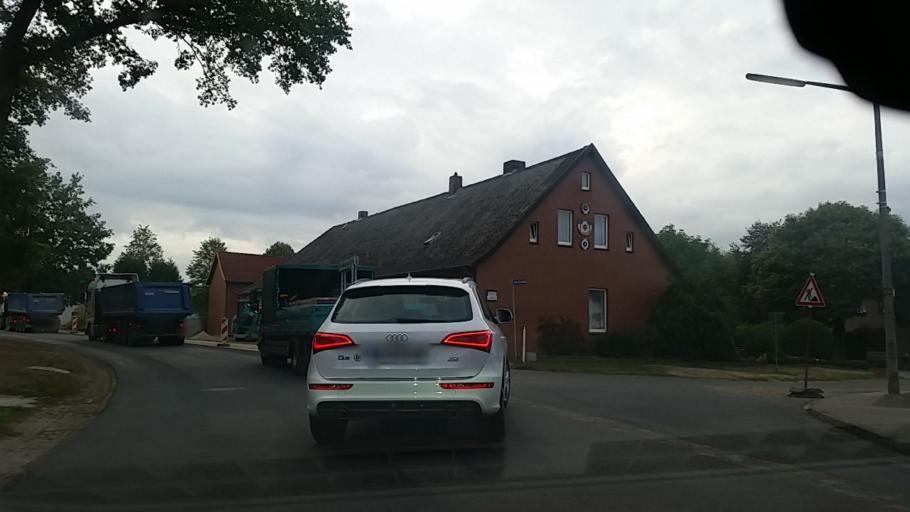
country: DE
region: Lower Saxony
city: Hankensbuttel
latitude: 52.7103
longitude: 10.6259
